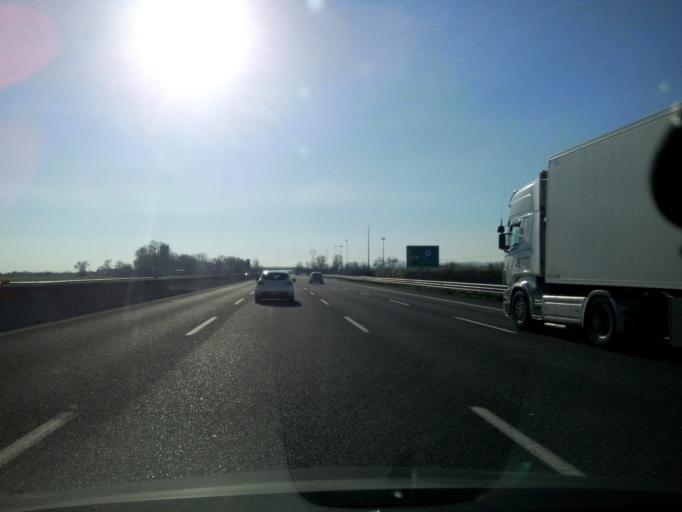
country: IT
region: Emilia-Romagna
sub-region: Provincia di Modena
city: San Cesario sul Panaro
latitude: 44.5608
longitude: 11.0541
